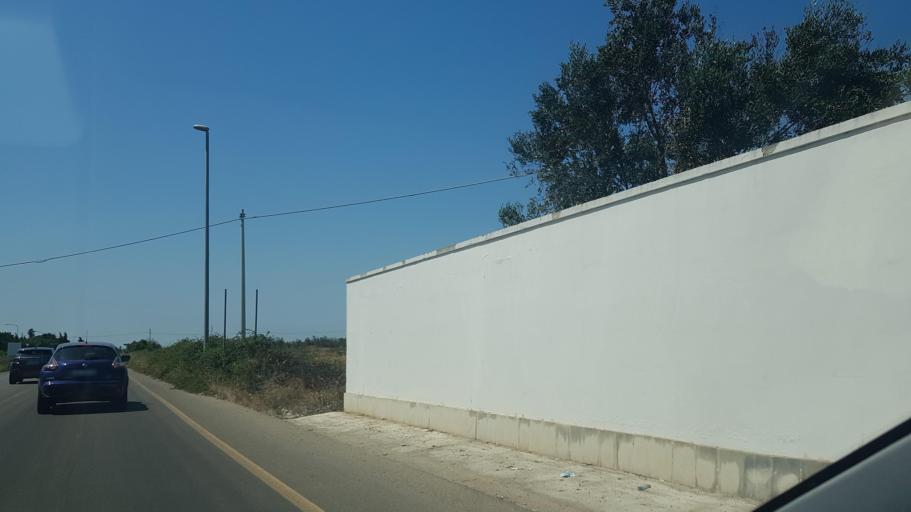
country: IT
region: Apulia
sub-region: Provincia di Lecce
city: Merine
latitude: 40.3363
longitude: 18.2331
